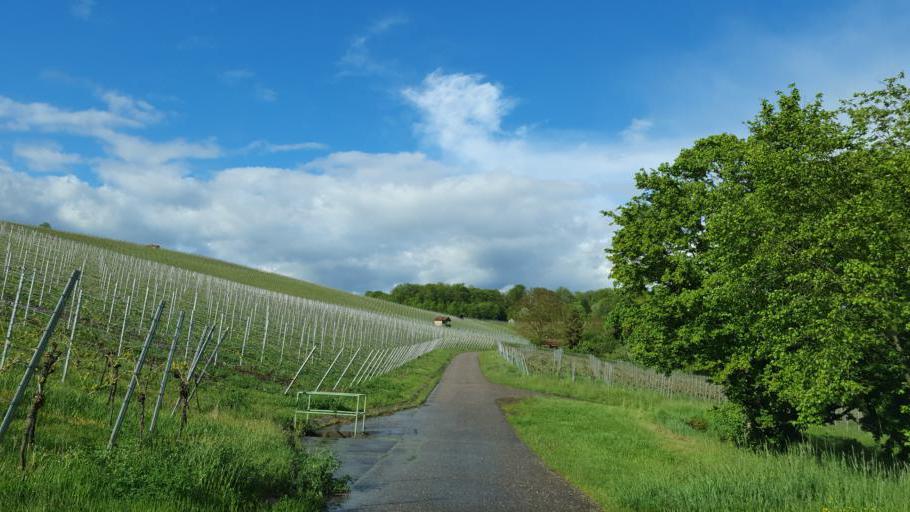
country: DE
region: Baden-Wuerttemberg
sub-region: Regierungsbezirk Stuttgart
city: Erlenbach
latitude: 49.1940
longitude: 9.2583
